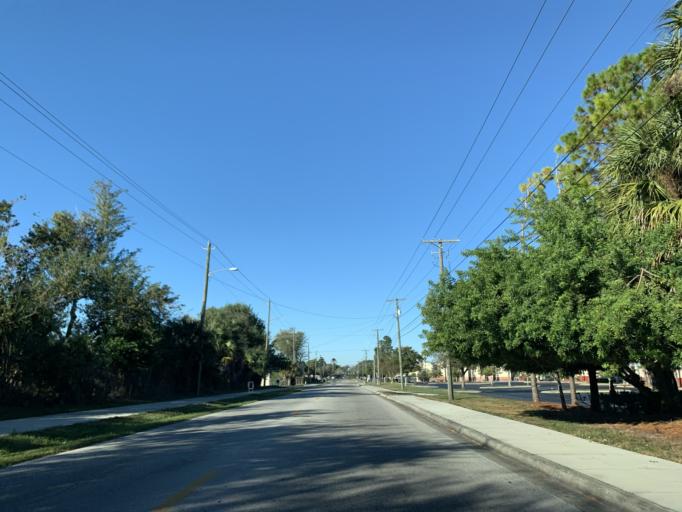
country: US
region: Florida
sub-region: Hillsborough County
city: University
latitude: 28.0436
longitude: -82.4228
